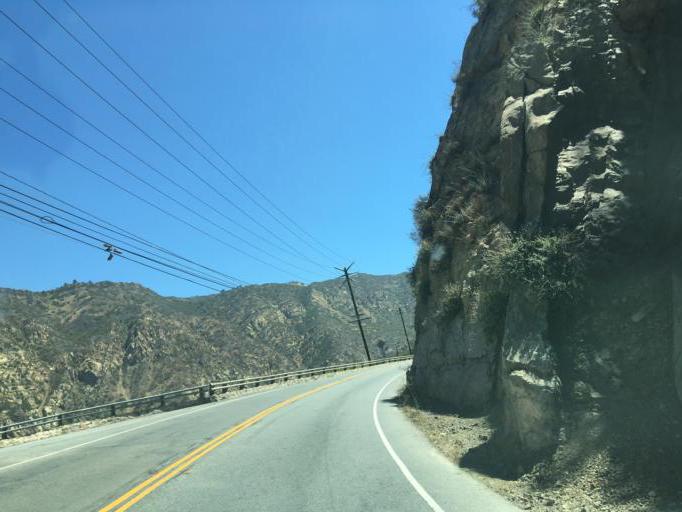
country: US
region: California
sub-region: Los Angeles County
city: Malibu Beach
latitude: 34.0637
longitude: -118.7027
